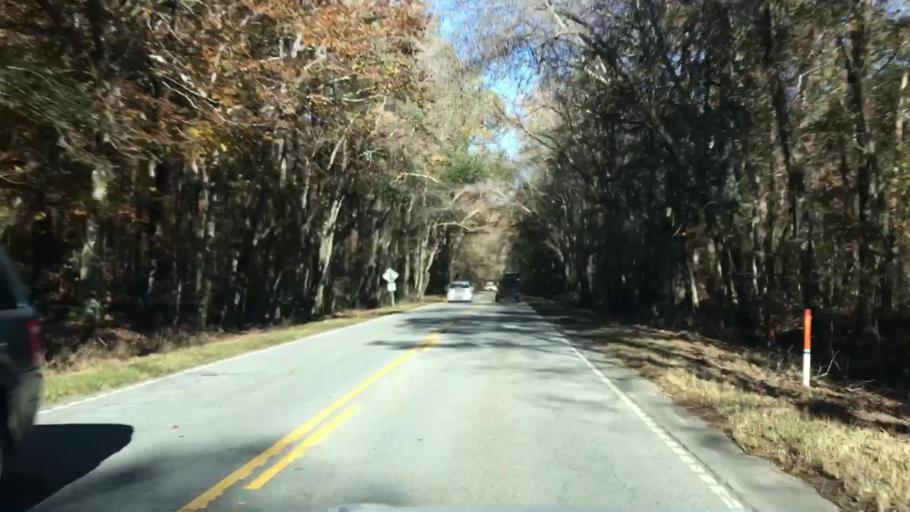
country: US
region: South Carolina
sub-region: Berkeley County
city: Ladson
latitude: 32.9061
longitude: -80.1471
